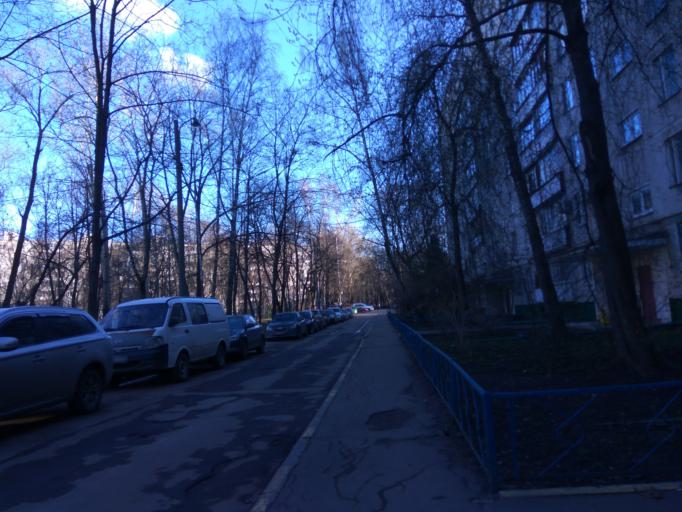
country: RU
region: Moscow
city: Veshnyaki
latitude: 55.7262
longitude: 37.8079
